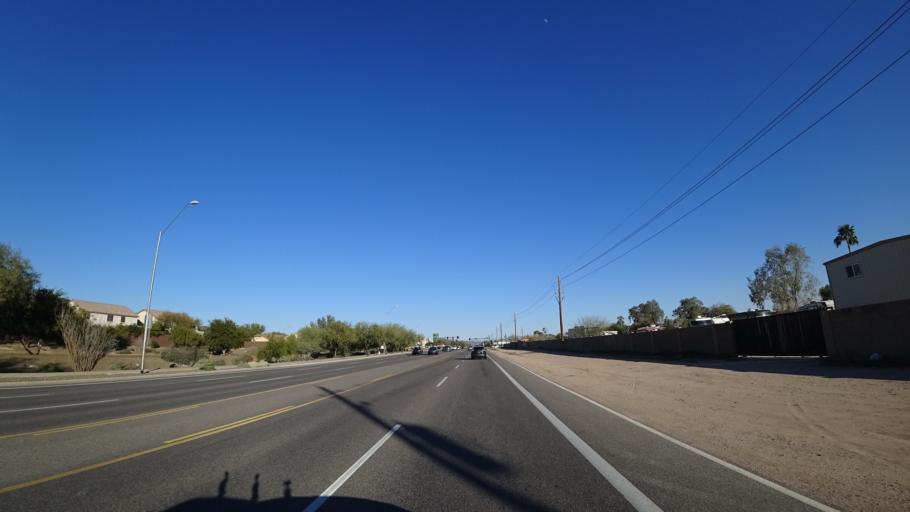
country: US
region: Arizona
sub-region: Maricopa County
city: Peoria
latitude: 33.7124
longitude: -112.1722
